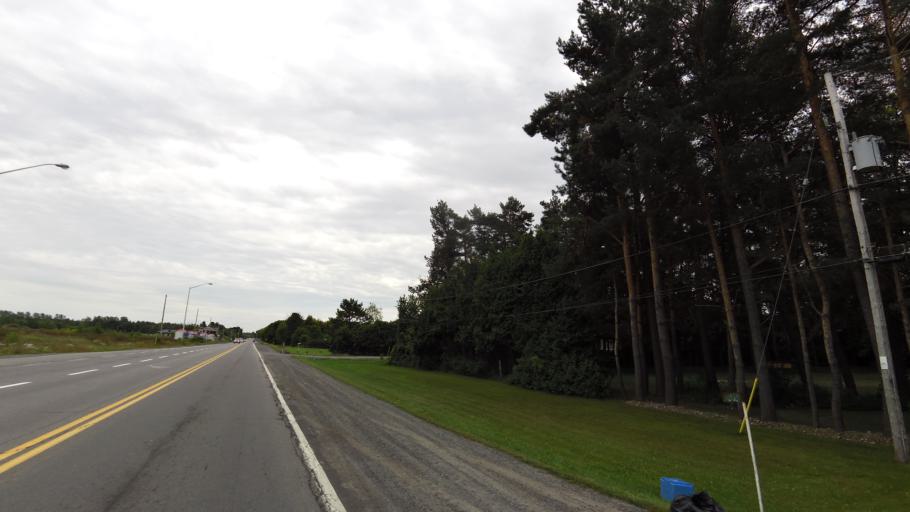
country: CA
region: Ontario
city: Ottawa
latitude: 45.2637
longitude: -75.5572
